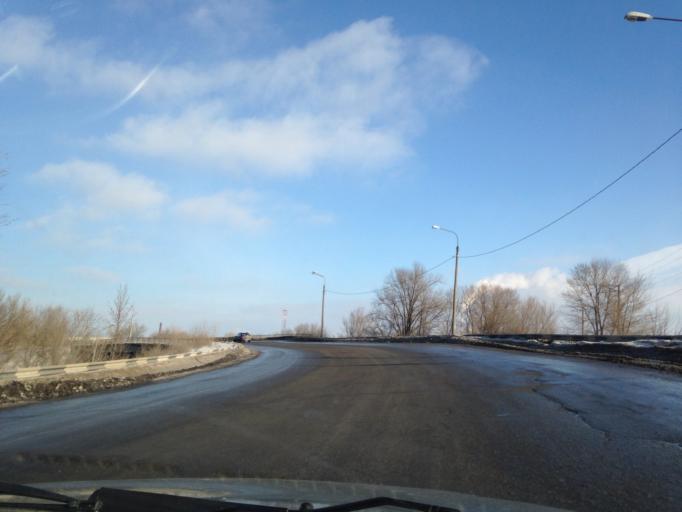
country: RU
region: Ulyanovsk
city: Mirnyy
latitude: 54.3376
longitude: 48.5639
